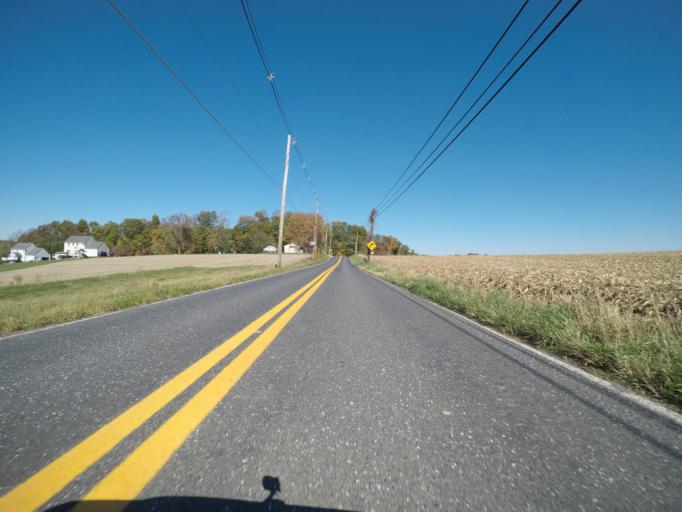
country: US
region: Maryland
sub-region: Carroll County
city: Hampstead
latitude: 39.5716
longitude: -76.8798
